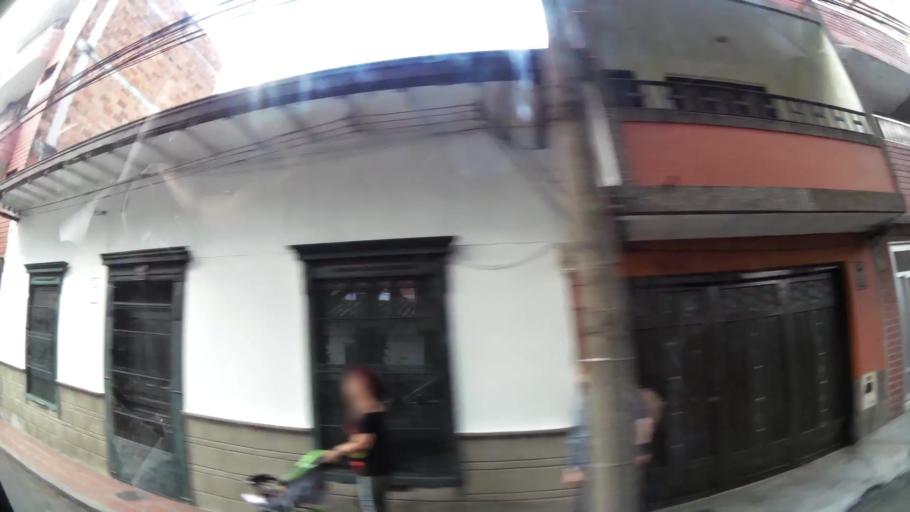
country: CO
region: Antioquia
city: Envigado
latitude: 6.1667
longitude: -75.5845
